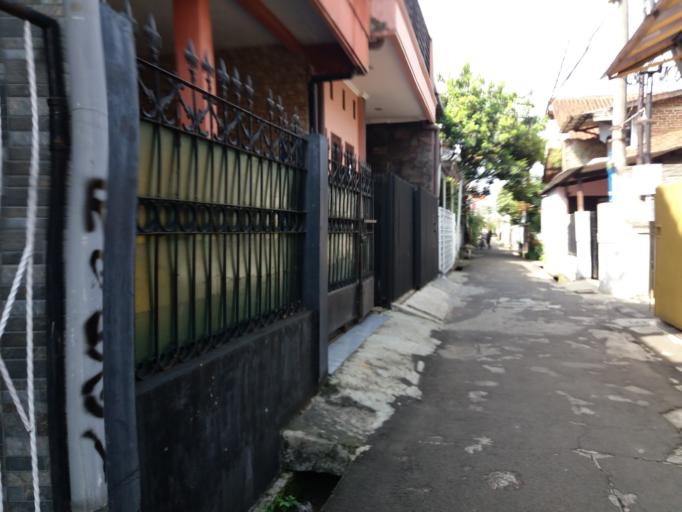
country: ID
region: West Java
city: Bandung
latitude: -6.9188
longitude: 107.6546
